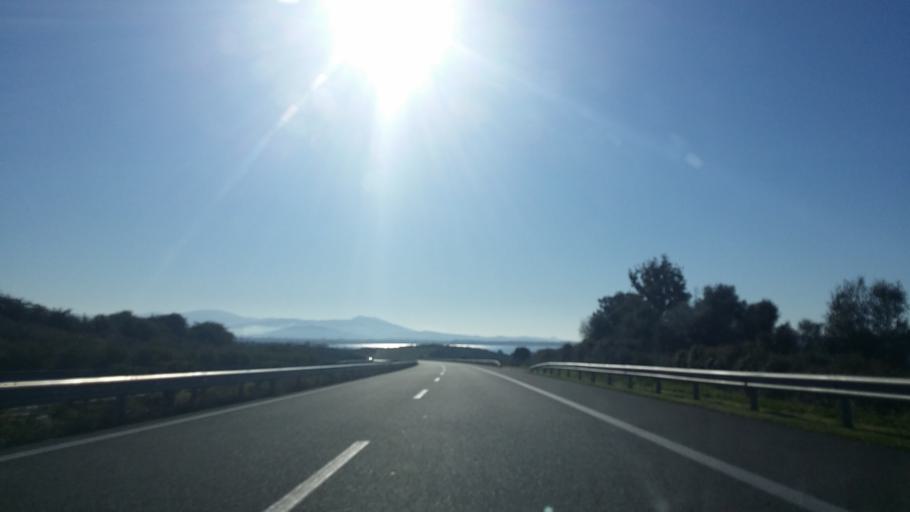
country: GR
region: West Greece
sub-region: Nomos Aitolias kai Akarnanias
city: Fitiai
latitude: 38.6832
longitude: 21.2171
